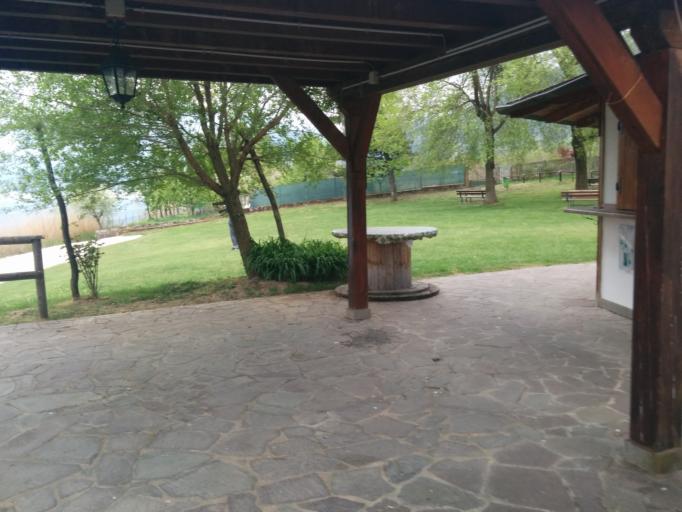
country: IT
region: Trentino-Alto Adige
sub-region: Provincia di Trento
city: Calceranica al Lago
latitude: 46.0310
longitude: 11.2323
